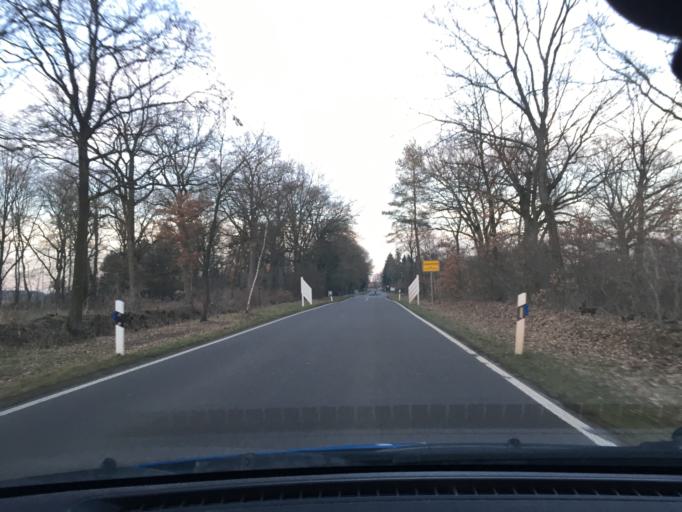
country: DE
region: Schleswig-Holstein
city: Langenlehsten
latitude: 53.4904
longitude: 10.7358
